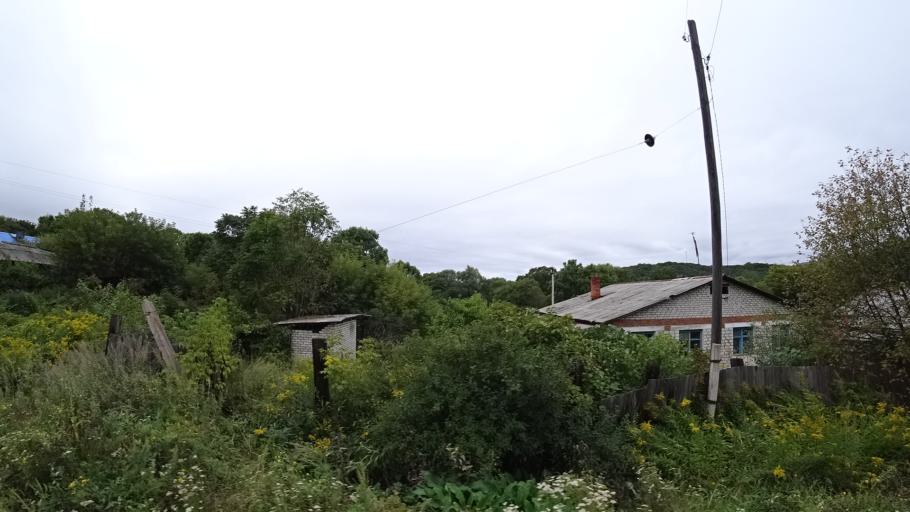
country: RU
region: Primorskiy
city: Rettikhovka
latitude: 44.1636
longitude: 132.7496
